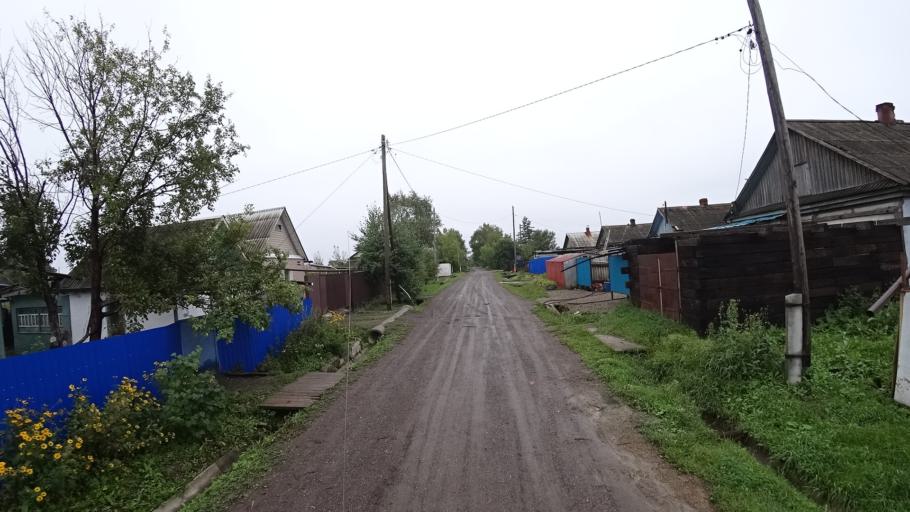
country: RU
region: Primorskiy
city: Monastyrishche
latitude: 44.2023
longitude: 132.4200
